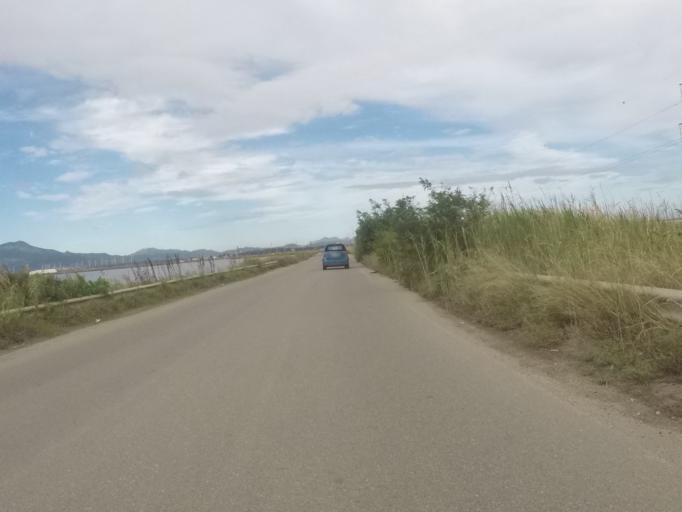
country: IT
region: Sardinia
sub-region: Provincia di Cagliari
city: Elmas
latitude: 39.2200
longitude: 9.0504
